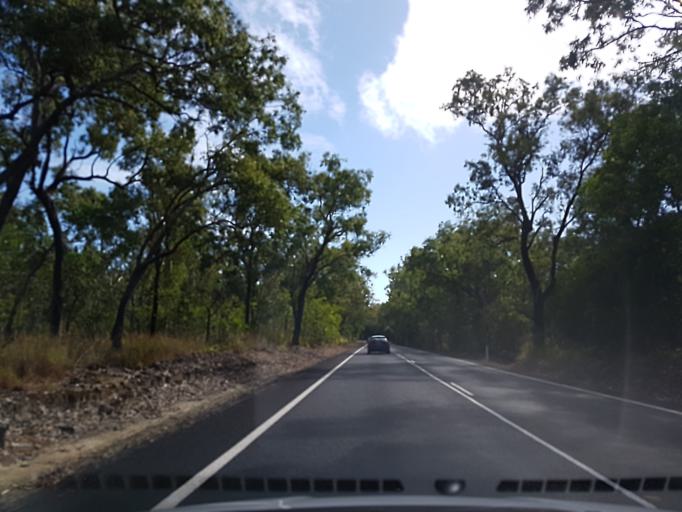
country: AU
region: Queensland
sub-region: Cairns
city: Palm Cove
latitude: -16.6696
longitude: 145.5680
